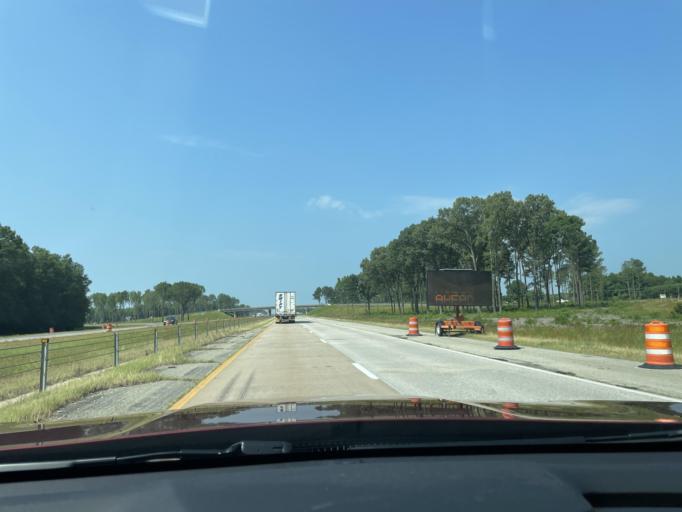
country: US
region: Arkansas
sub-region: White County
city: Searcy
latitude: 35.2065
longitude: -91.7296
